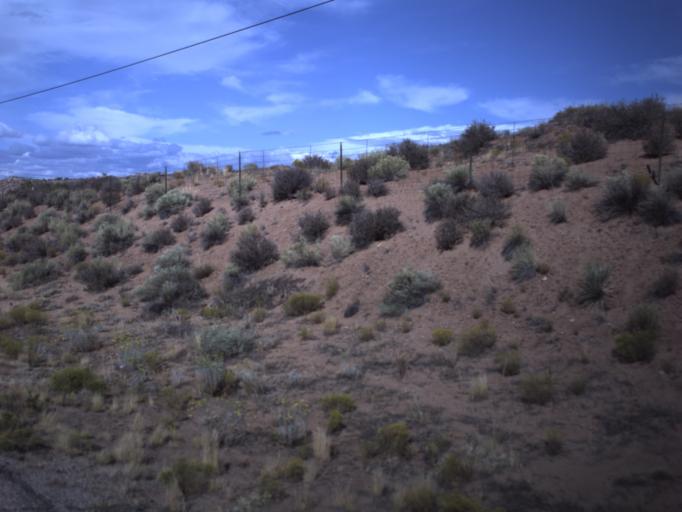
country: US
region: Utah
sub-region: San Juan County
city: Blanding
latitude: 37.2940
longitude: -109.2872
